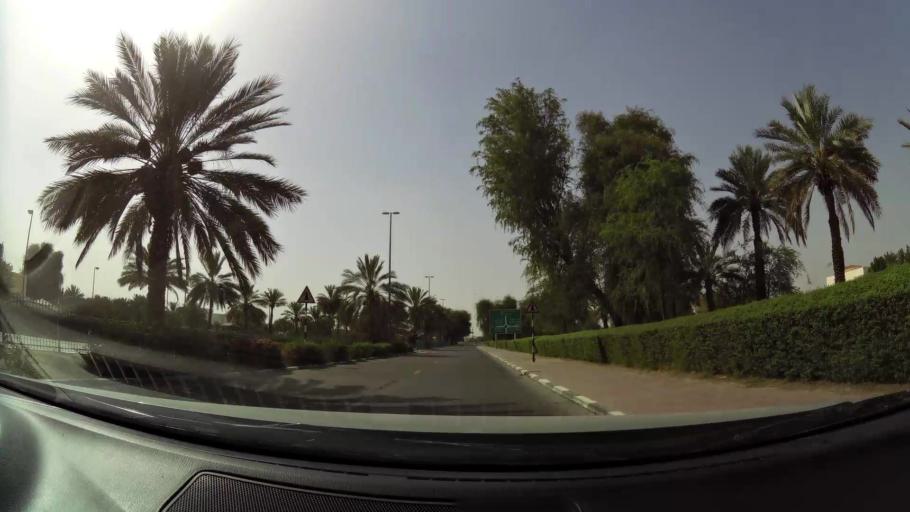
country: AE
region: Abu Dhabi
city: Al Ain
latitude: 24.2351
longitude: 55.6911
